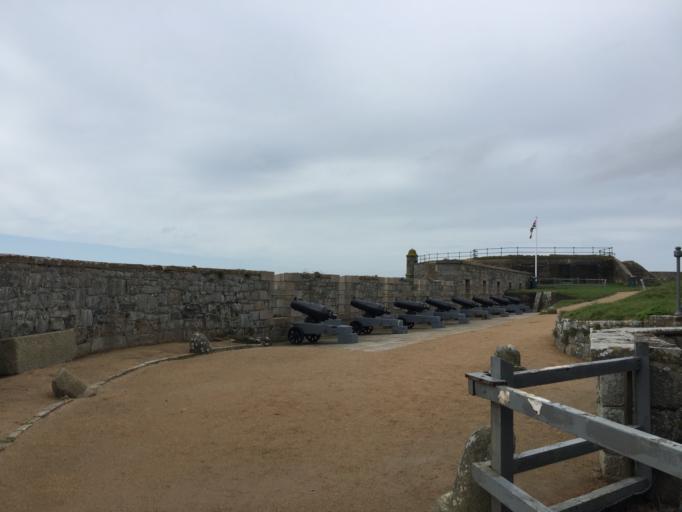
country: JE
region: St Helier
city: Saint Helier
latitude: 49.1767
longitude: -2.1252
